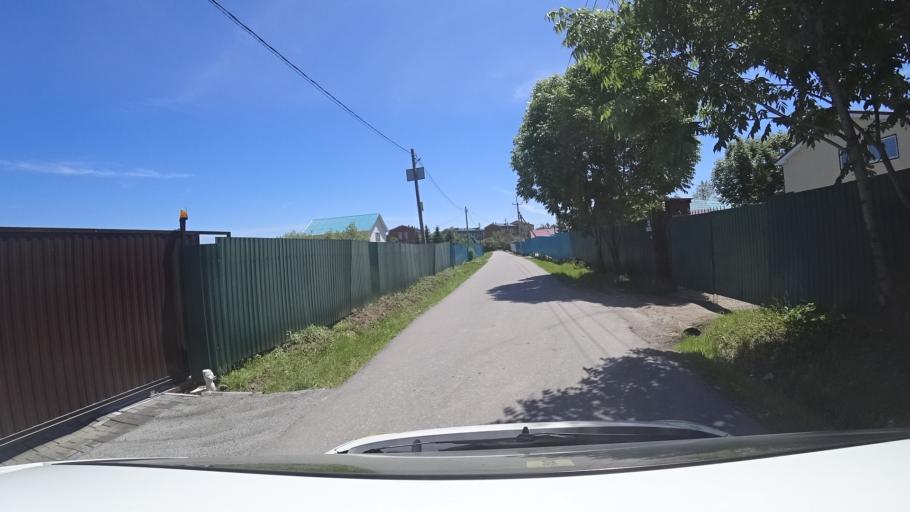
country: RU
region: Khabarovsk Krai
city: Topolevo
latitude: 48.5079
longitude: 135.1794
